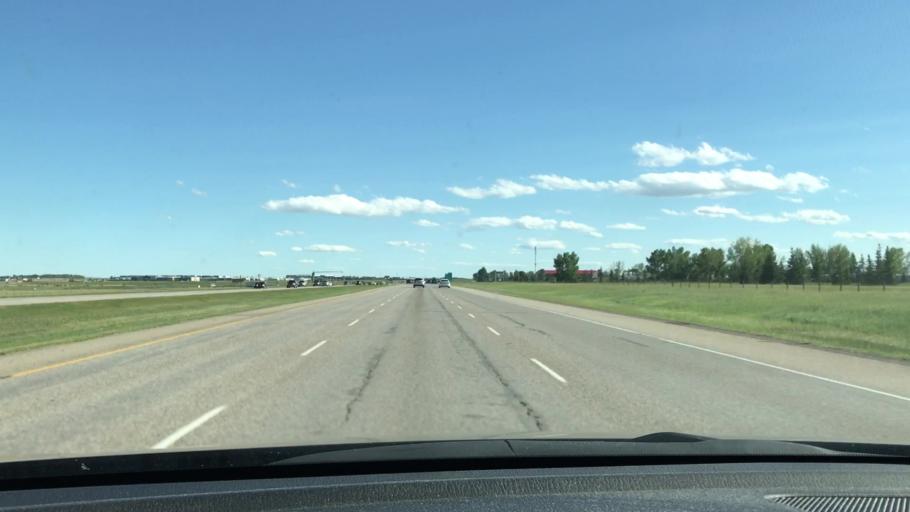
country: CA
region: Alberta
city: Airdrie
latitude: 51.2269
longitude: -114.0018
